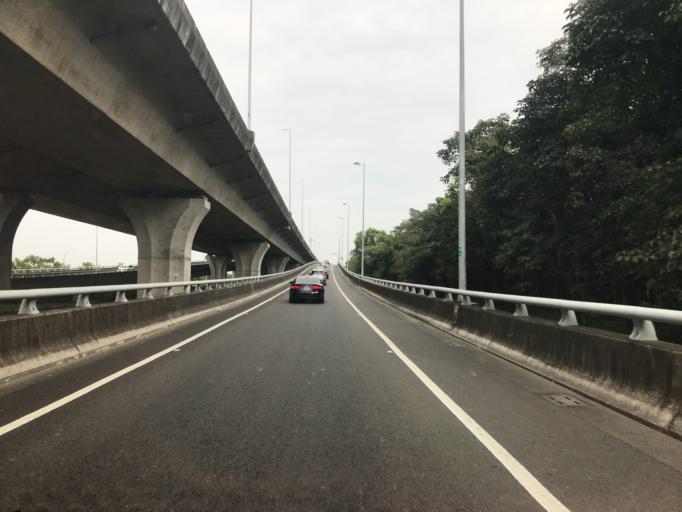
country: TW
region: Taiwan
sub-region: Pingtung
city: Pingtung
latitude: 22.6455
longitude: 120.5421
